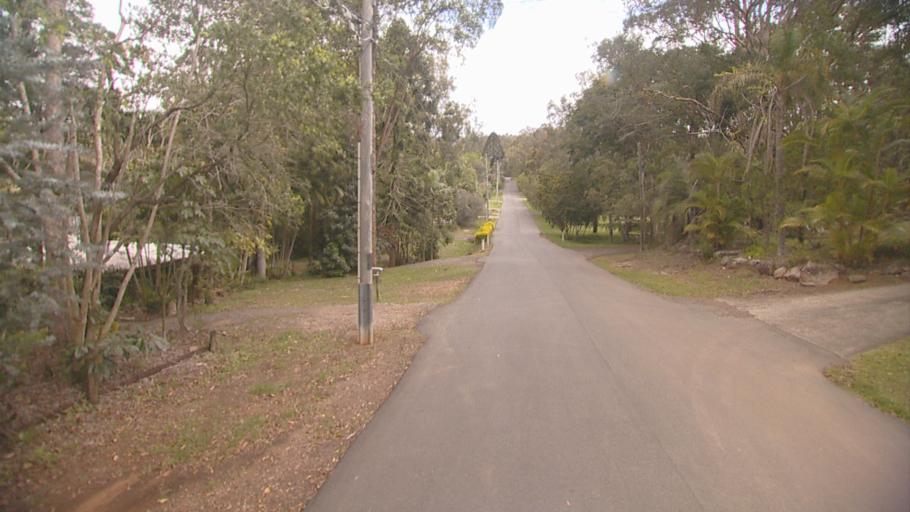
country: AU
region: Queensland
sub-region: Logan
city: Slacks Creek
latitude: -27.6682
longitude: 153.1715
